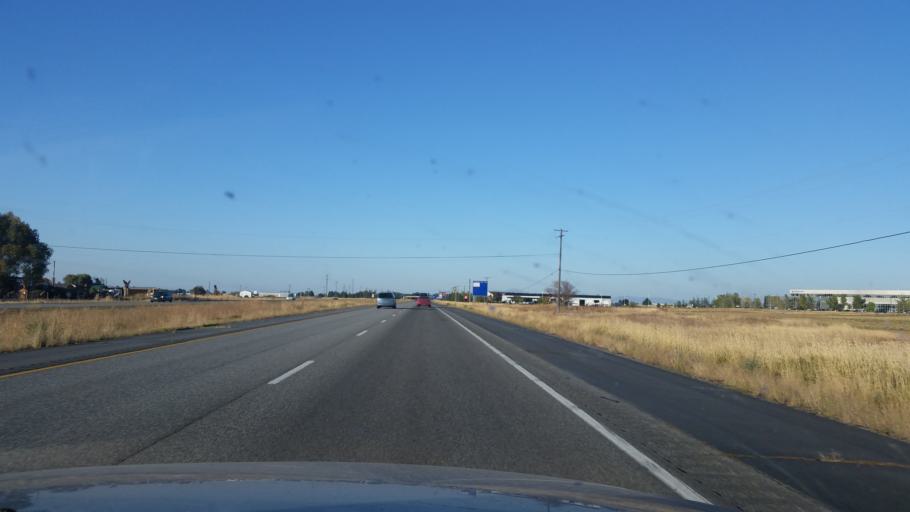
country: US
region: Washington
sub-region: Spokane County
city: Airway Heights
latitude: 47.5813
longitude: -117.5762
